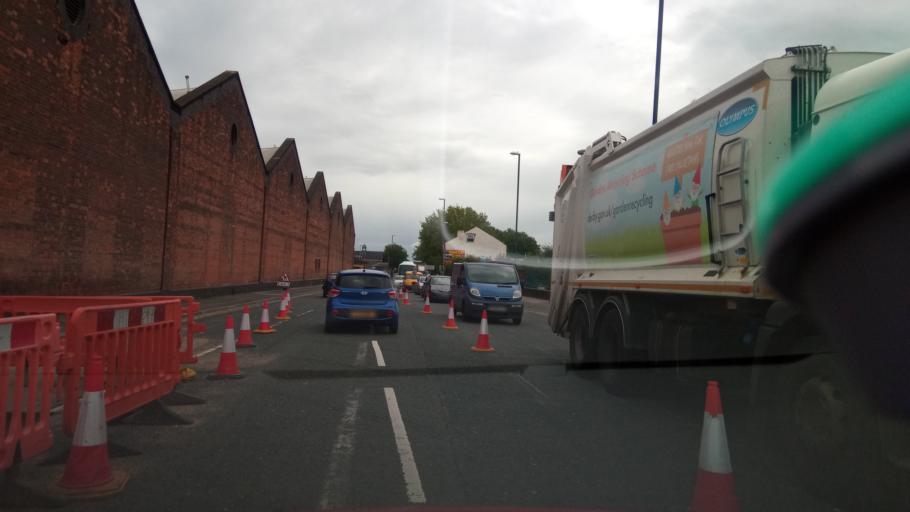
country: GB
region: England
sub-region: Derby
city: Derby
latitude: 52.9060
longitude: -1.4628
